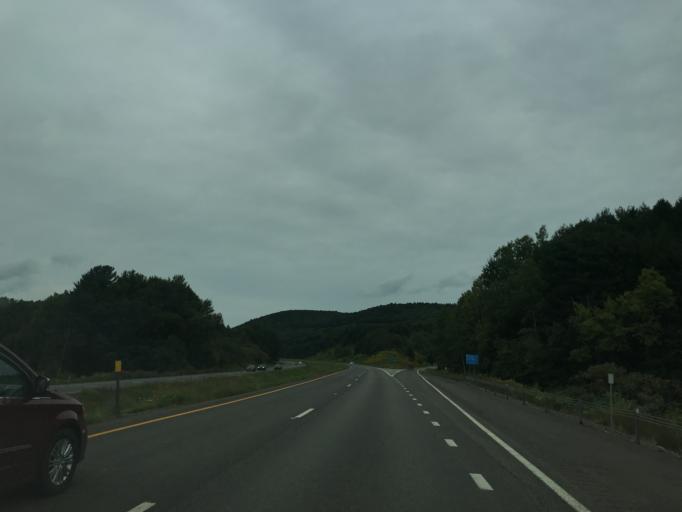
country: US
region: New York
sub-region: Otsego County
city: Unadilla
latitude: 42.3099
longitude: -75.3338
